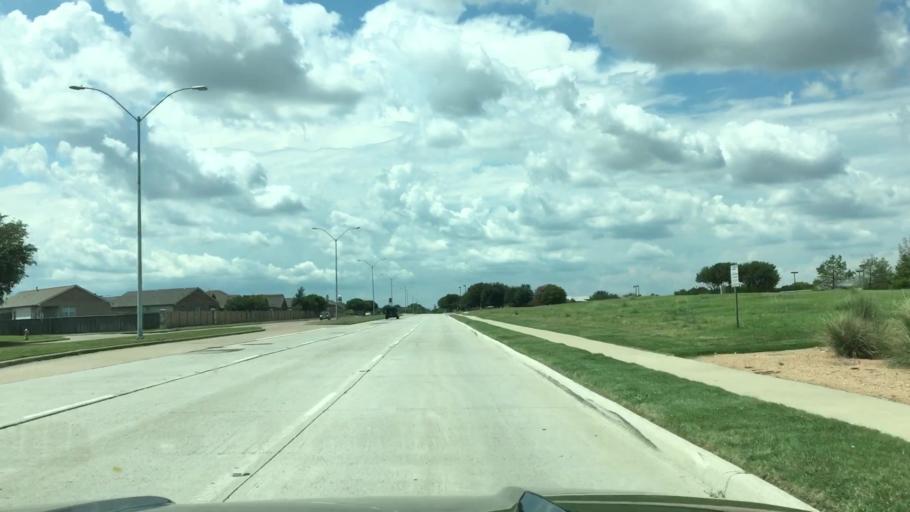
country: US
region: Texas
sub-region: Tarrant County
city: Blue Mound
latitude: 32.8614
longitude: -97.3262
